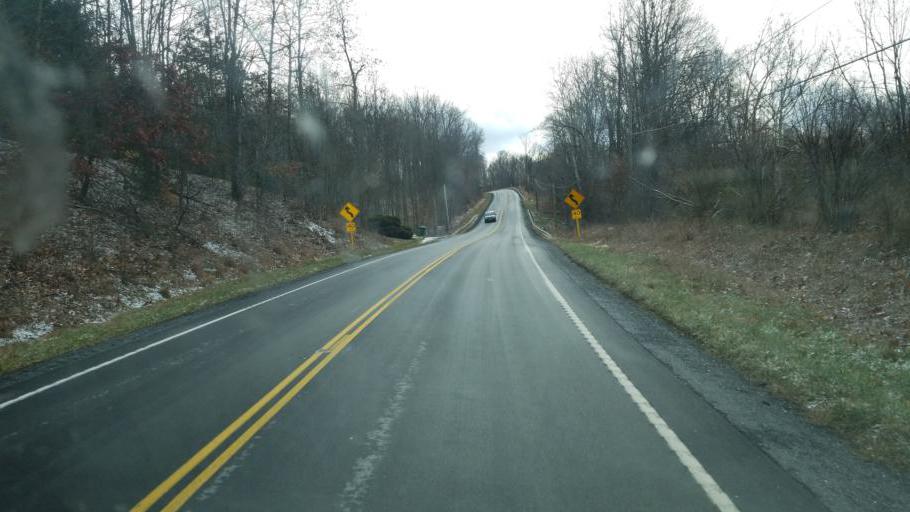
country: US
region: Ohio
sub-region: Muskingum County
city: Frazeysburg
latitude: 40.1185
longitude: -82.1859
